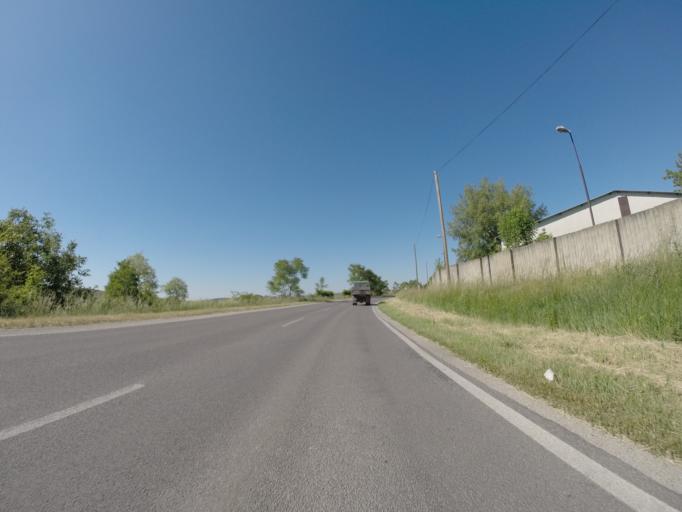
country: SK
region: Trnavsky
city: Hlohovec
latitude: 48.3823
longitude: 17.7969
